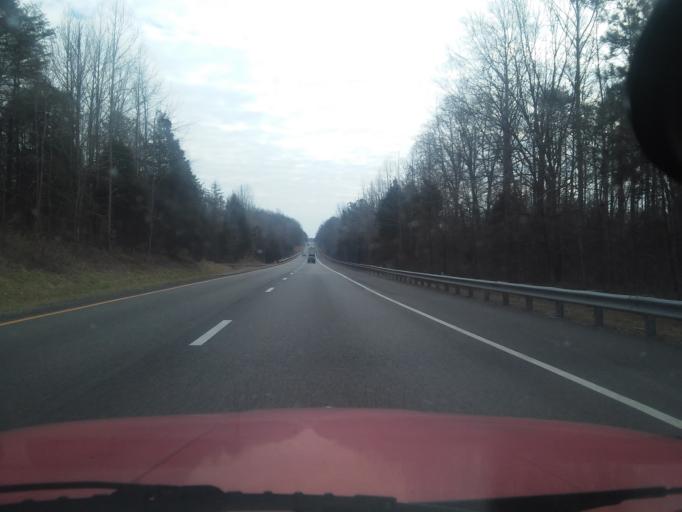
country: US
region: Virginia
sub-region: Goochland County
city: Goochland
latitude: 37.7762
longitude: -77.8828
